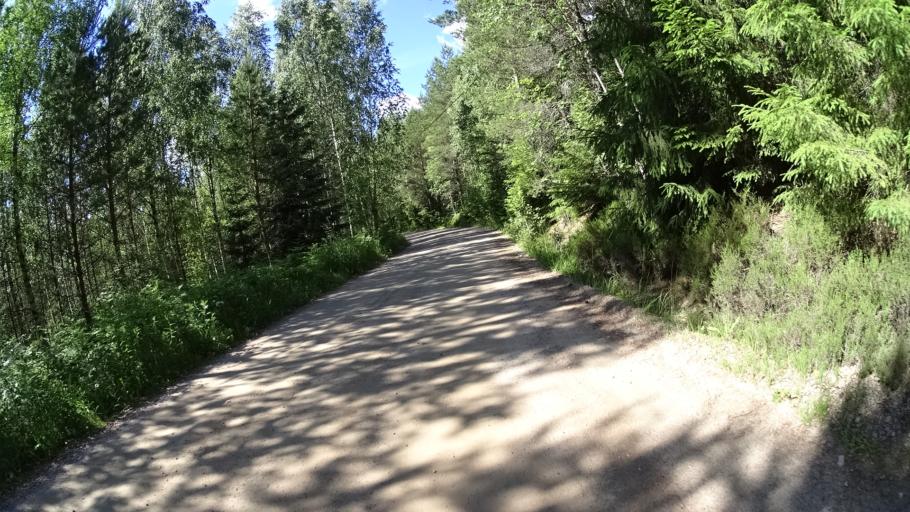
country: FI
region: Uusimaa
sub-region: Helsinki
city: Vihti
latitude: 60.3108
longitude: 24.4395
